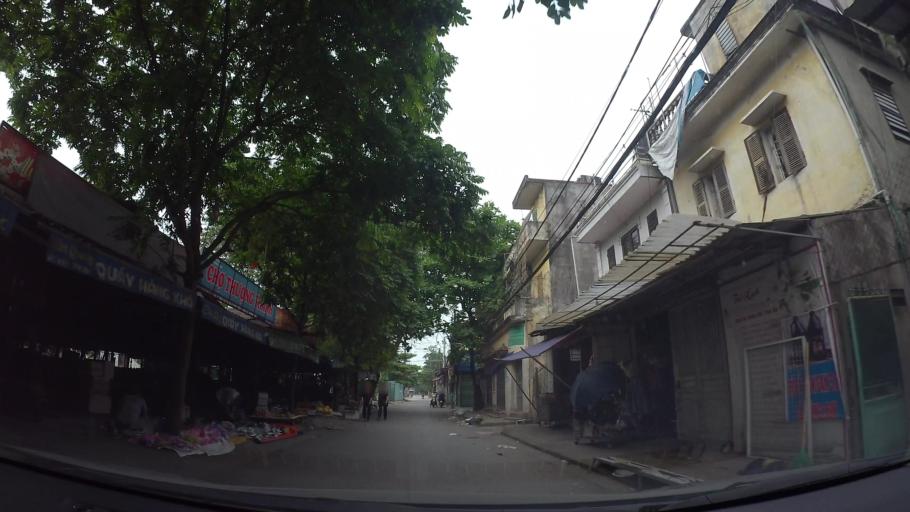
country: VN
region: Ha Noi
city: Hoan Kiem
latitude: 21.0643
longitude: 105.8842
